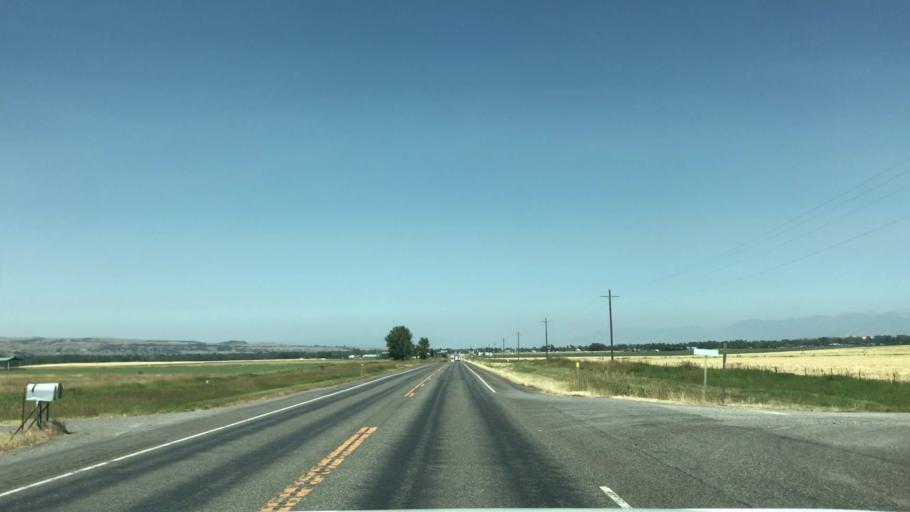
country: US
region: Montana
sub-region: Gallatin County
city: Four Corners
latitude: 45.5672
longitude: -111.1968
